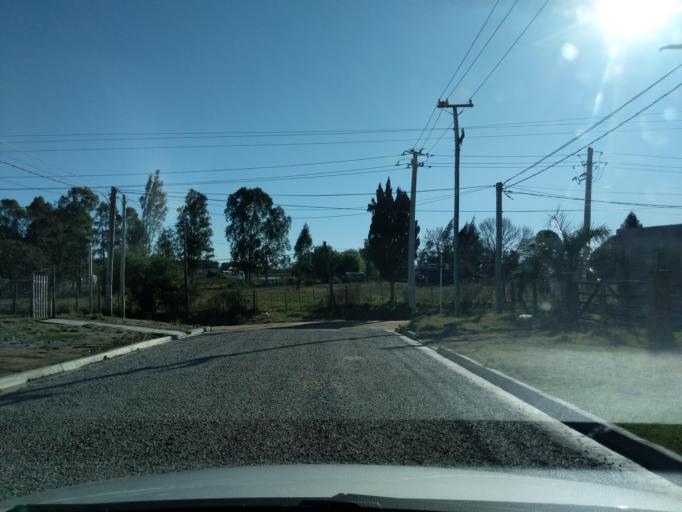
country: UY
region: Florida
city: Florida
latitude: -34.0853
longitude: -56.2384
